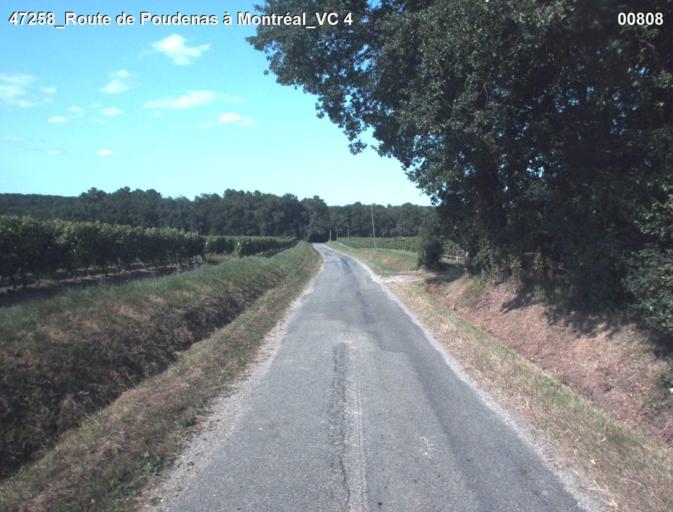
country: FR
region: Midi-Pyrenees
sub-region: Departement du Gers
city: Montreal
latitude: 44.0102
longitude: 0.1866
